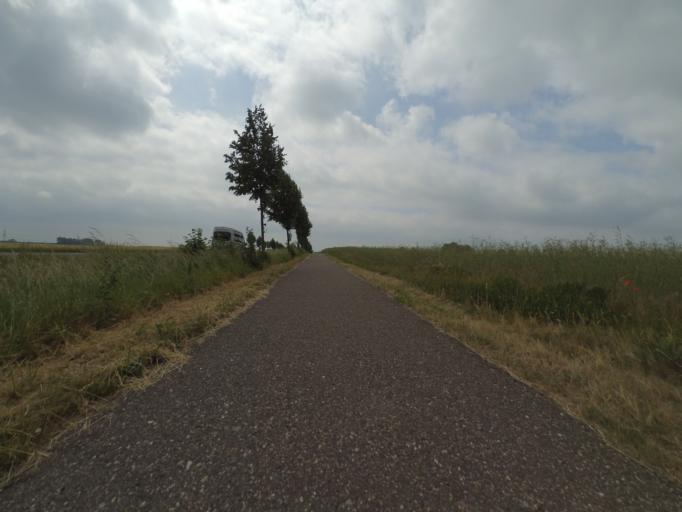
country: DE
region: Mecklenburg-Vorpommern
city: Malchow
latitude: 53.5235
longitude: 12.4230
